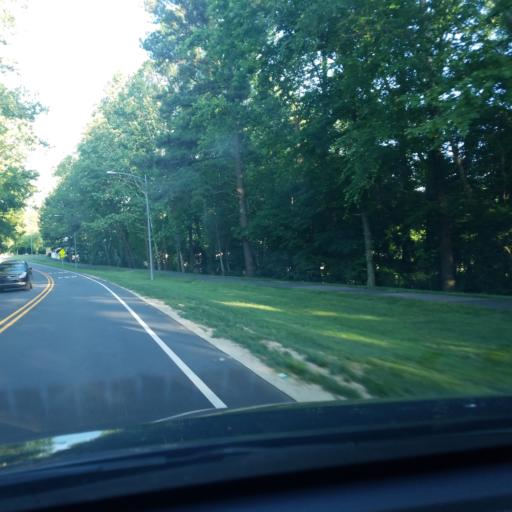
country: US
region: North Carolina
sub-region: Durham County
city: Durham
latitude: 35.9225
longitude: -78.9522
